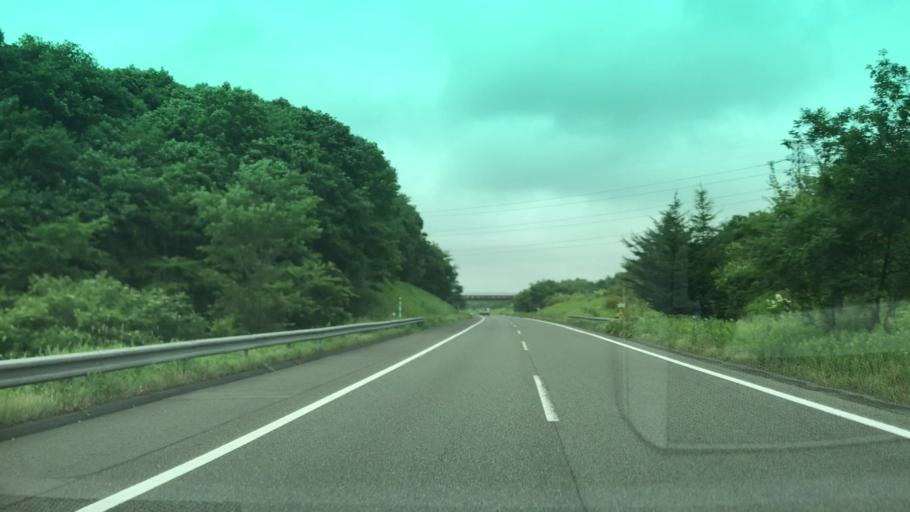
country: JP
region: Hokkaido
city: Chitose
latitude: 42.7364
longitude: 141.6522
